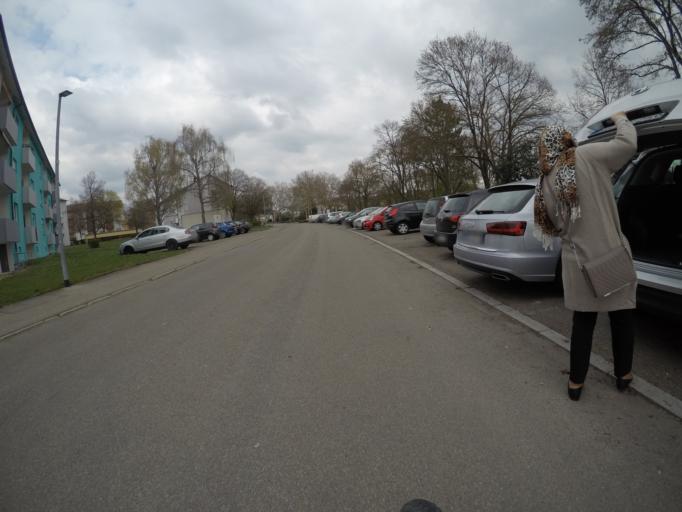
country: DE
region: Baden-Wuerttemberg
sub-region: Regierungsbezirk Stuttgart
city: Boeblingen
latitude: 48.6801
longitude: 9.0004
